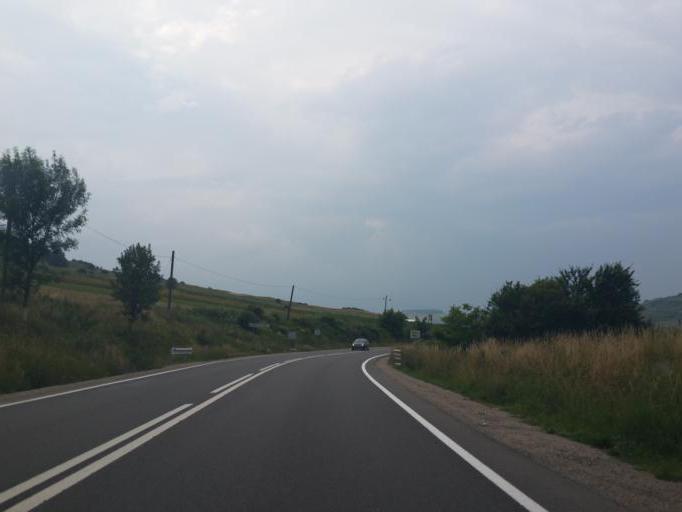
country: RO
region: Cluj
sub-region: Comuna Baciu
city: Mera
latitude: 46.8017
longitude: 23.4574
